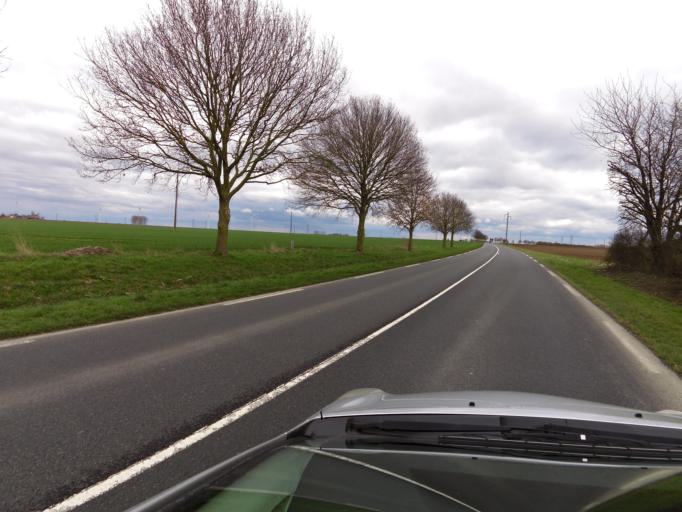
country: FR
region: Picardie
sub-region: Departement de la Somme
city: Roye
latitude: 49.7203
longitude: 2.8067
